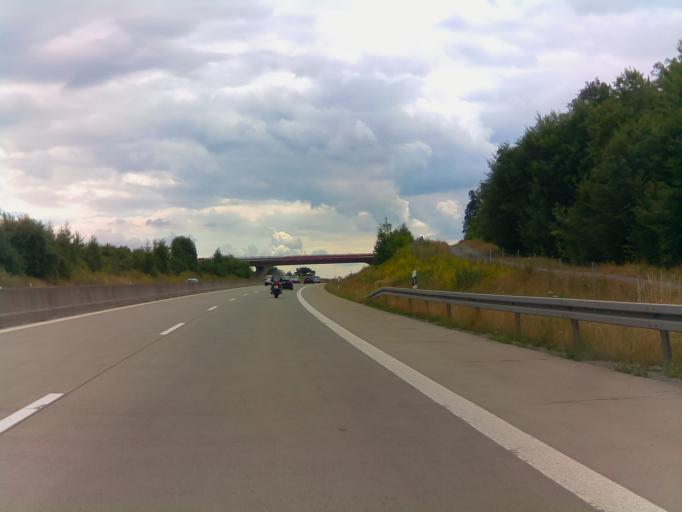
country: DE
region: Bavaria
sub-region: Regierungsbezirk Unterfranken
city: Rodelmaier
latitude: 50.2977
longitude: 10.2760
